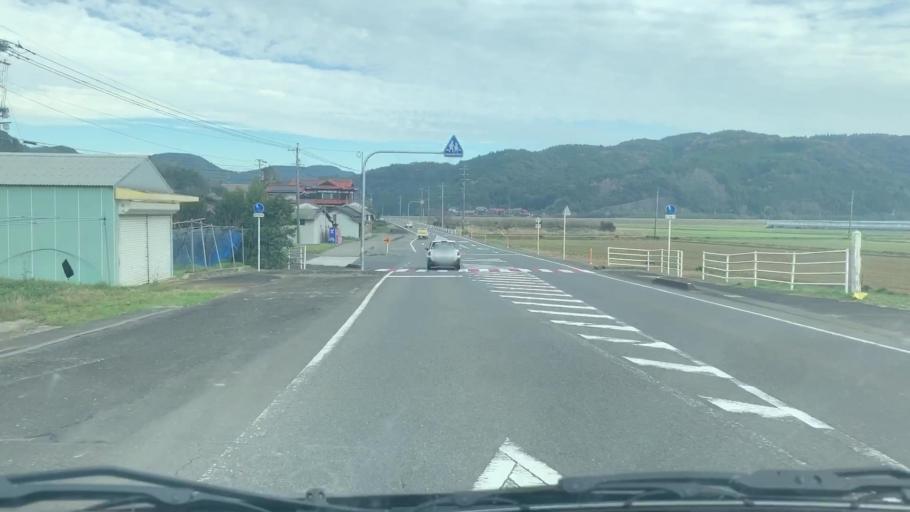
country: JP
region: Saga Prefecture
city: Imaricho-ko
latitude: 33.3098
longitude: 129.9709
